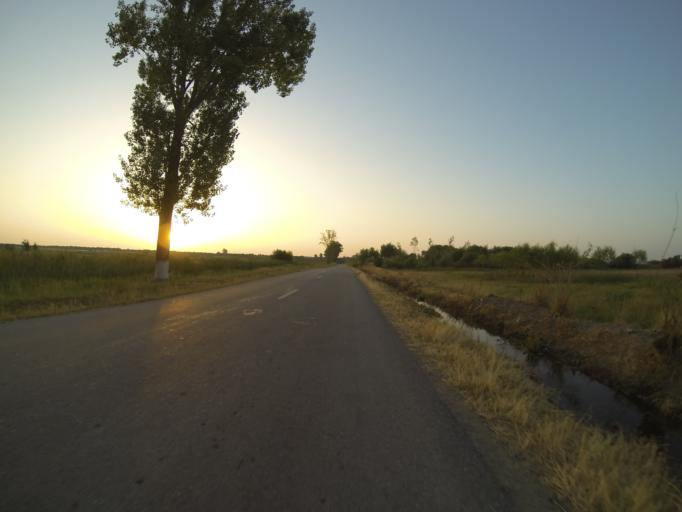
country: RO
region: Dolj
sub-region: Comuna Dobresti
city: Dobresti
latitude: 43.9828
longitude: 23.9291
